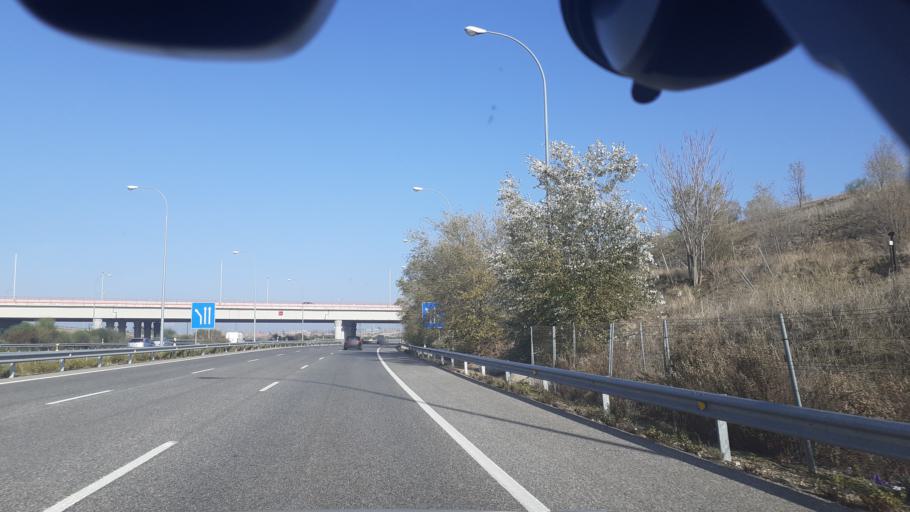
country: ES
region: Madrid
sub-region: Provincia de Madrid
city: Coslada
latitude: 40.4070
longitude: -3.5678
